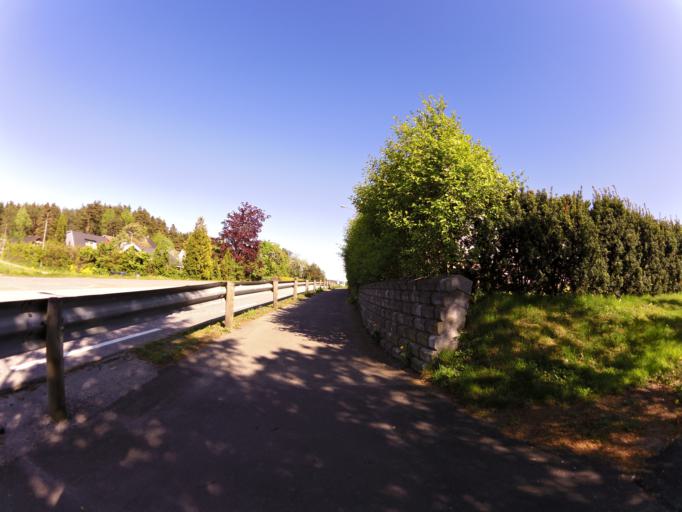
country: NO
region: Ostfold
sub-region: Fredrikstad
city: Fredrikstad
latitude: 59.2301
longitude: 11.0181
